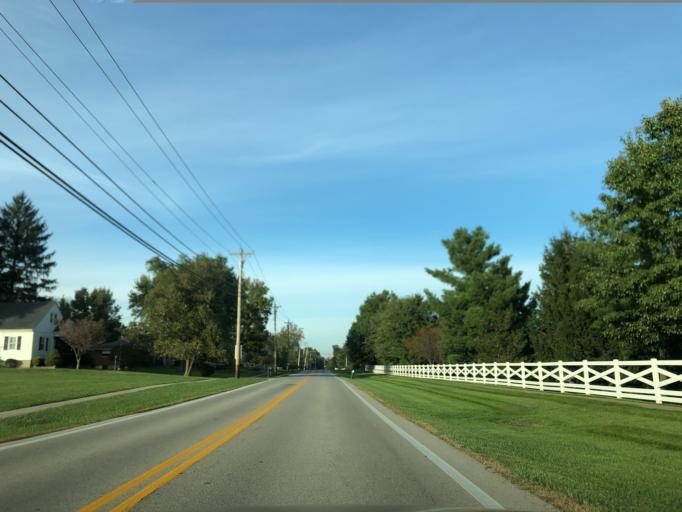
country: US
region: Ohio
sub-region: Hamilton County
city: Loveland
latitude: 39.2800
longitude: -84.2723
